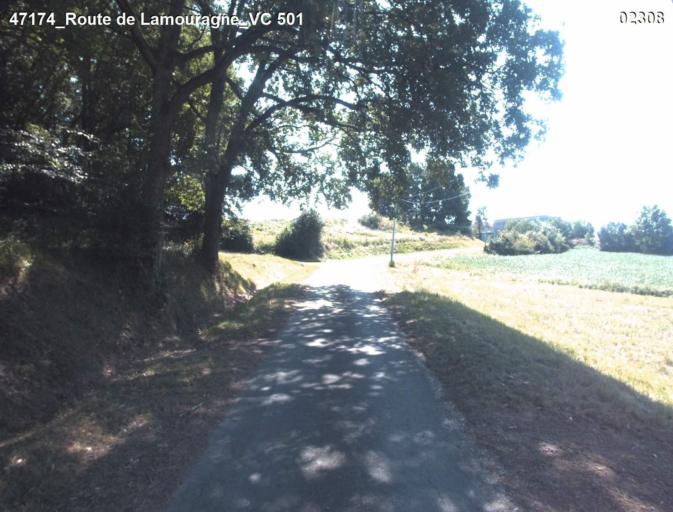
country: FR
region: Midi-Pyrenees
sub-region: Departement du Gers
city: Condom
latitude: 44.0287
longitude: 0.3953
